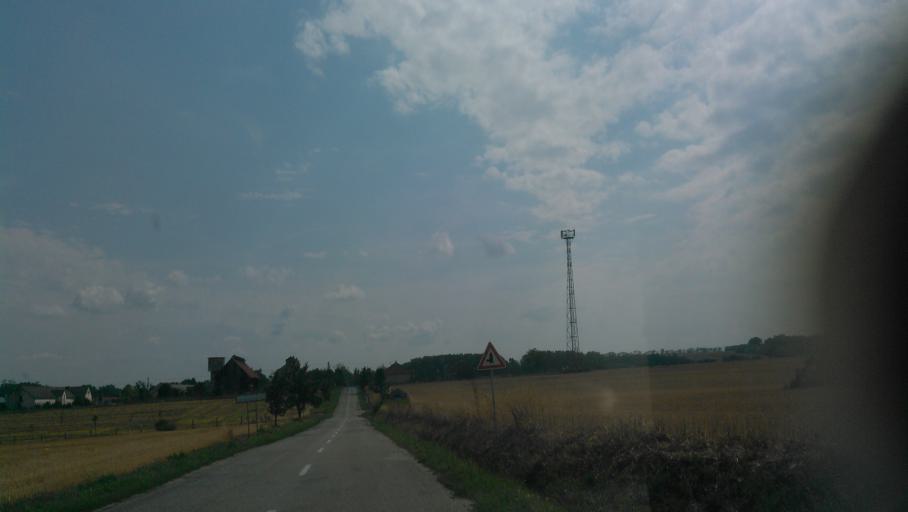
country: SK
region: Nitriansky
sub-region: Okres Nitra
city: Nitra
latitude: 48.4716
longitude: 18.0247
